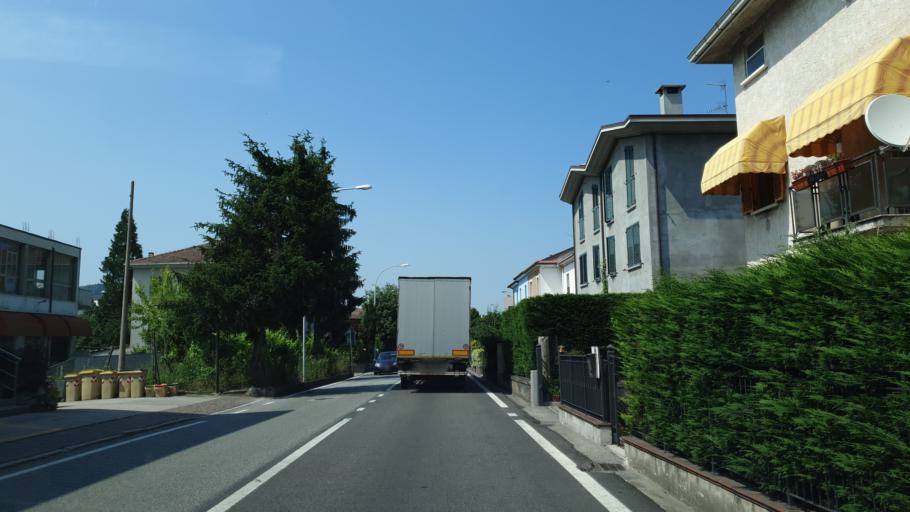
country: SM
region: Acquaviva
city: Acquaviva
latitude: 43.9528
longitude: 12.4057
